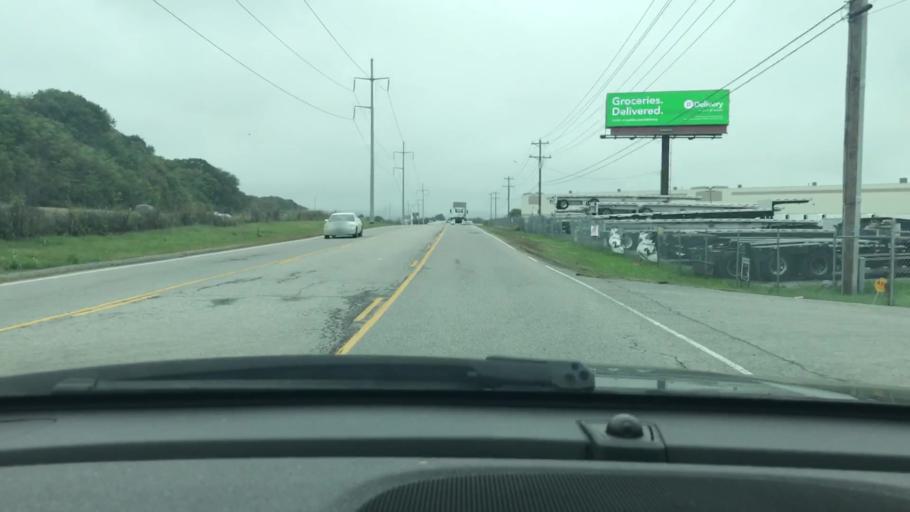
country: US
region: Tennessee
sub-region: Rutherford County
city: La Vergne
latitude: 35.9847
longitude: -86.5797
